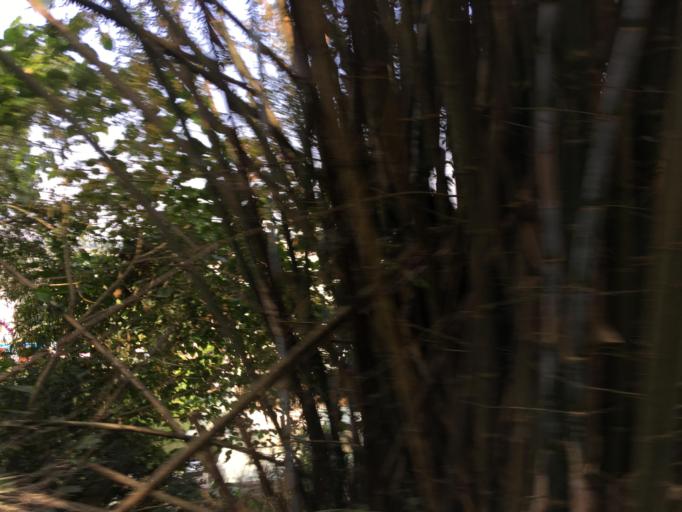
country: TW
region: Taiwan
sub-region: Chiayi
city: Jiayi Shi
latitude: 23.4933
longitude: 120.4880
